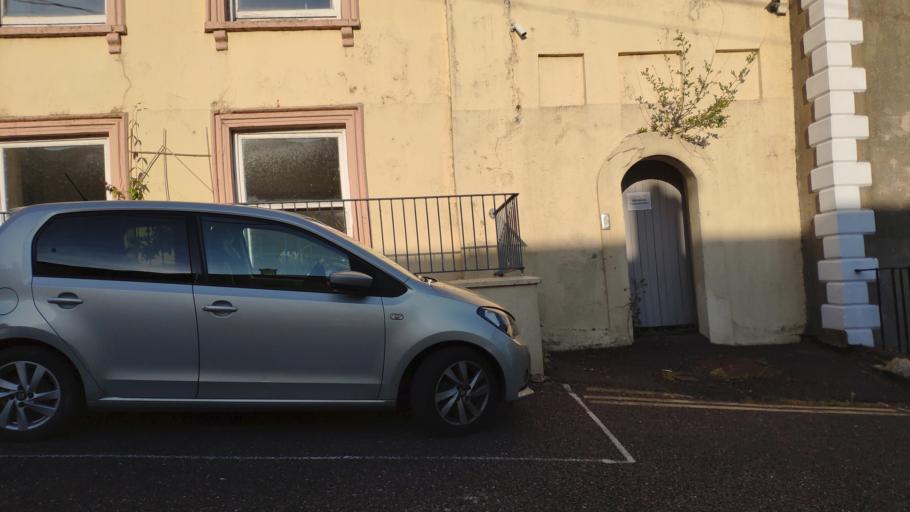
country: IE
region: Munster
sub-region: County Cork
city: Cork
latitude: 51.9039
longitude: -8.4697
